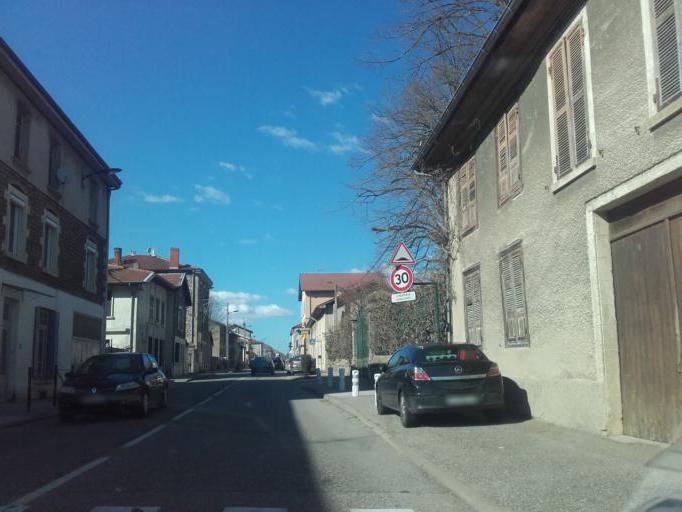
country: FR
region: Rhone-Alpes
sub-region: Departement de l'Isere
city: Champier
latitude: 45.4502
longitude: 5.2900
